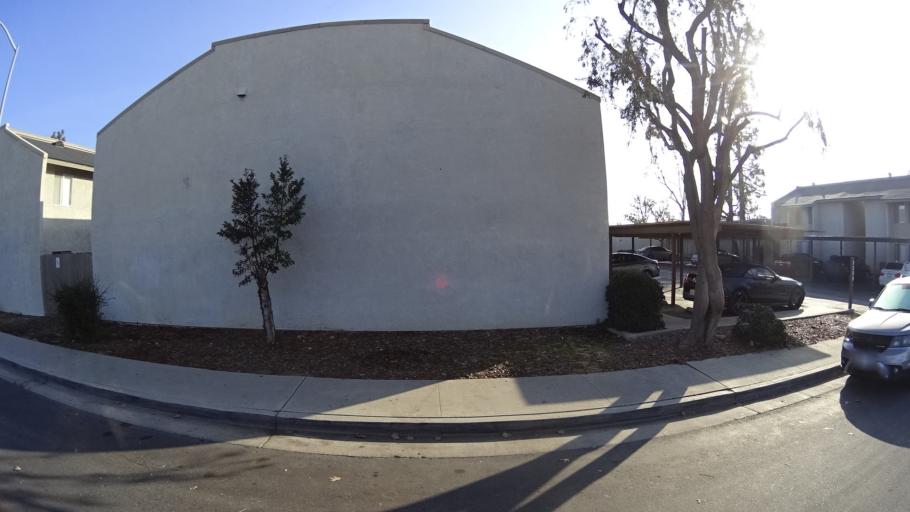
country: US
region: California
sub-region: Kern County
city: Oildale
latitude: 35.4011
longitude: -118.9310
